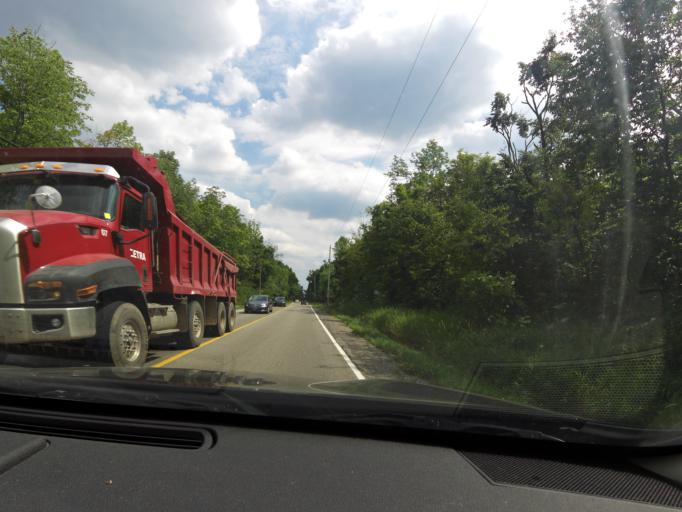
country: CA
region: Ontario
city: Orangeville
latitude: 43.7669
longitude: -79.9665
